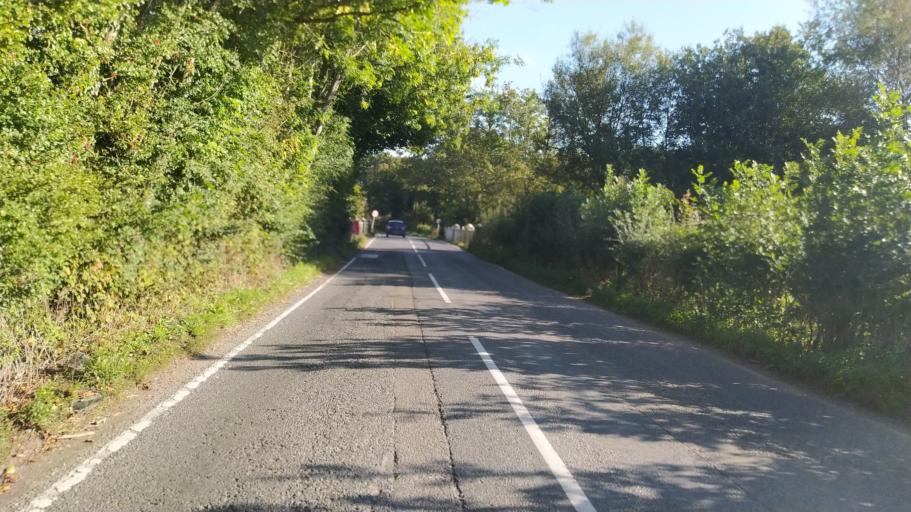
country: GB
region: England
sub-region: Hampshire
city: Romsey
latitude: 51.0084
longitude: -1.5006
